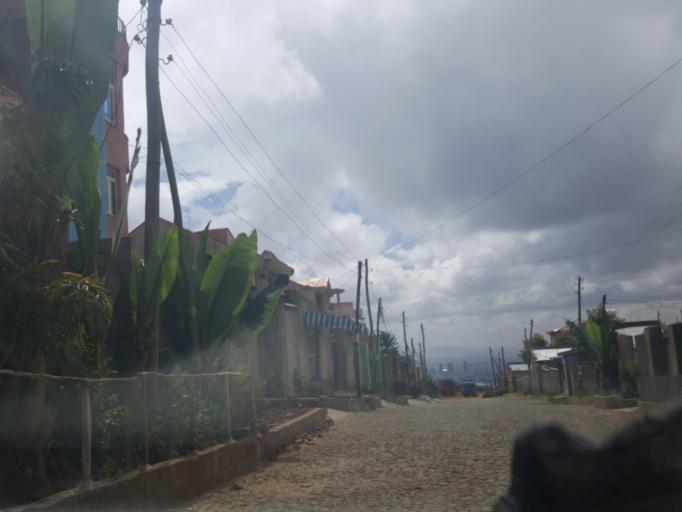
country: ET
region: Adis Abeba
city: Addis Ababa
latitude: 9.0688
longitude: 38.7407
